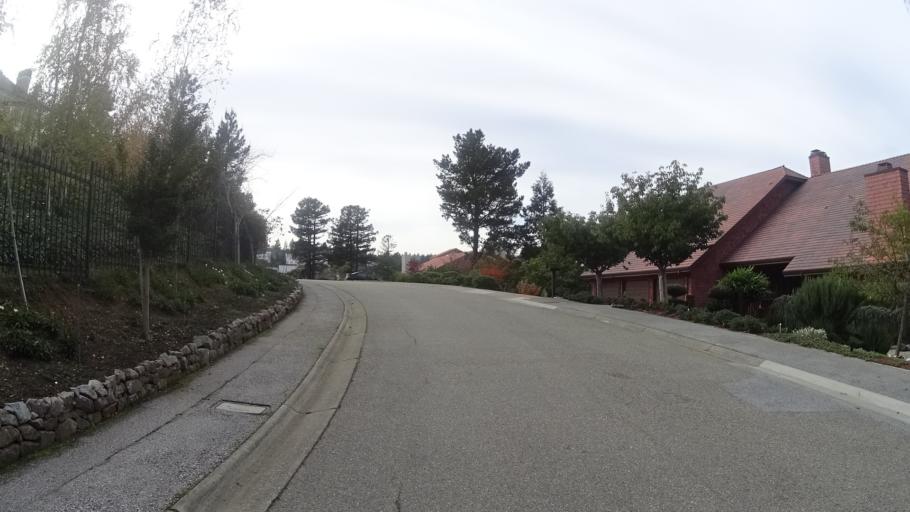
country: US
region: California
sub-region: San Mateo County
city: Hillsborough
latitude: 37.5683
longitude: -122.3794
